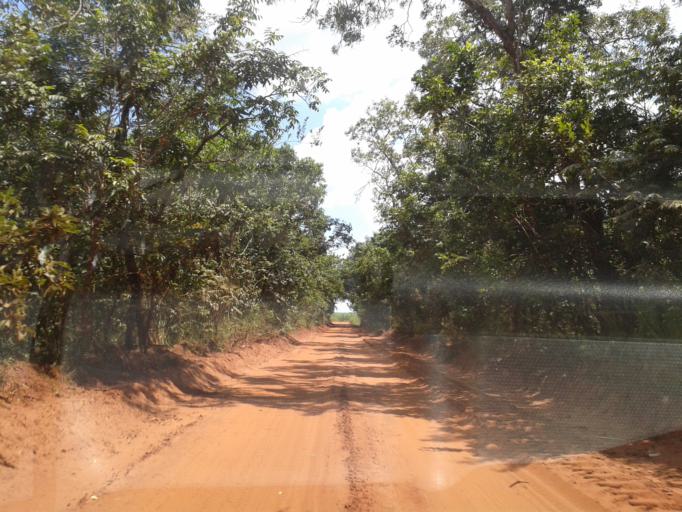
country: BR
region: Minas Gerais
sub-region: Ituiutaba
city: Ituiutaba
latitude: -19.0847
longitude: -49.7331
